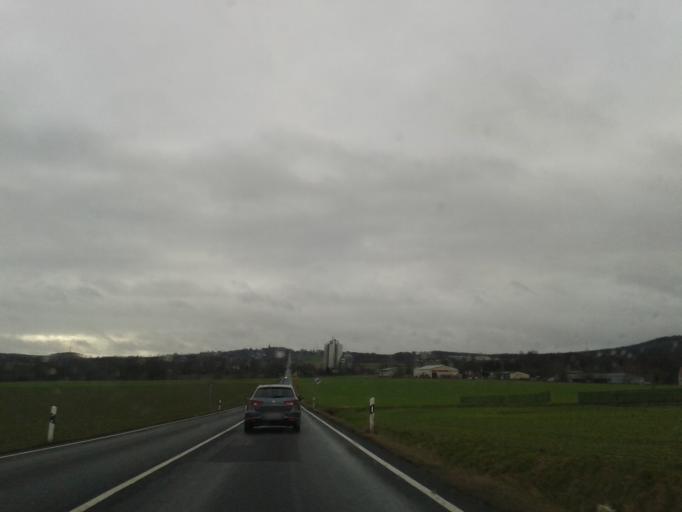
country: DE
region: Saxony
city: Grossschweidnitz
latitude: 51.0599
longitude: 14.6442
